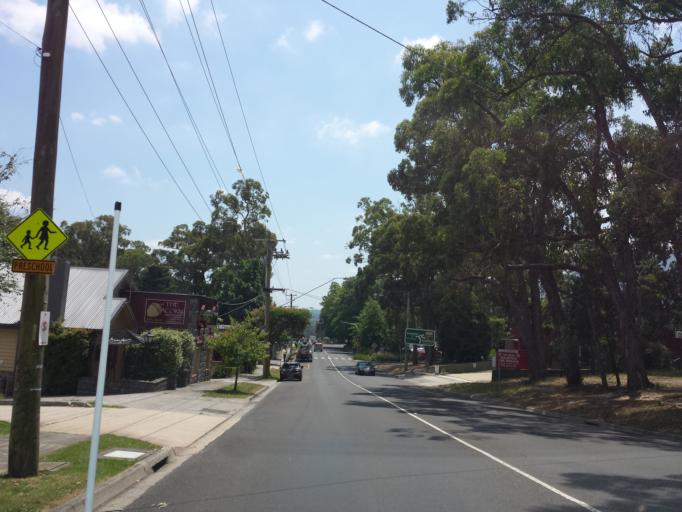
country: AU
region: Victoria
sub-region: Knox
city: The Basin
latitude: -37.8572
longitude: 145.3144
